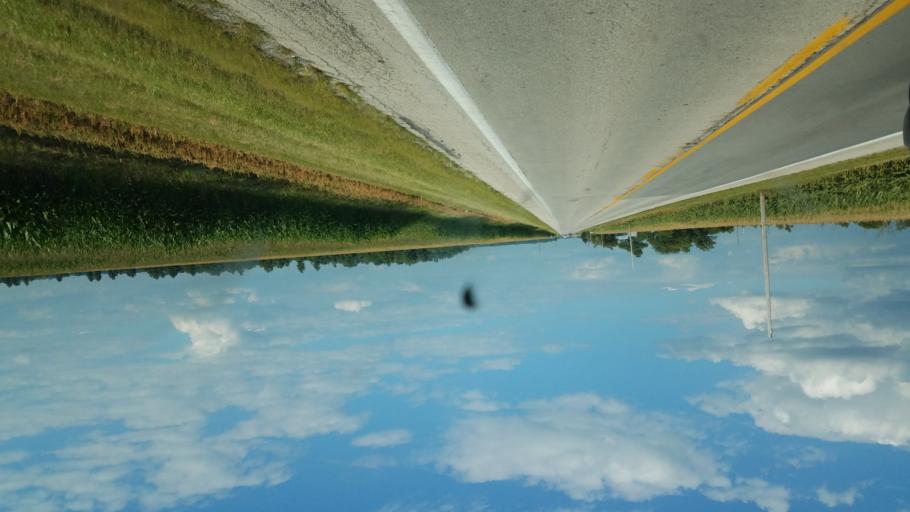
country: US
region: Ohio
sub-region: Wood County
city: Pemberville
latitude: 41.3549
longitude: -83.4710
